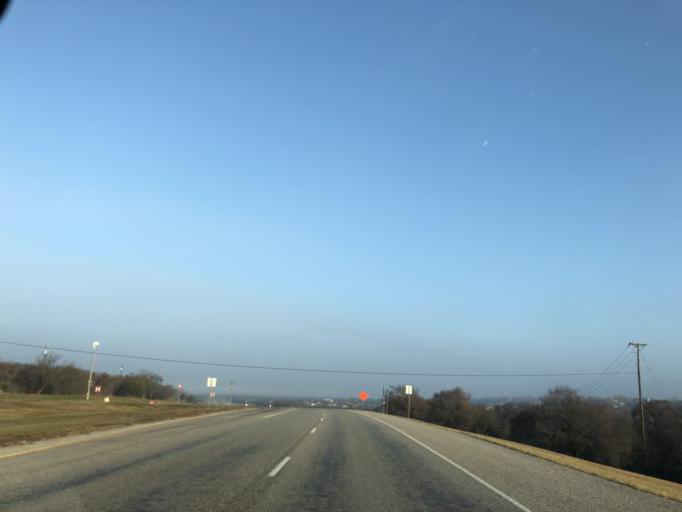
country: US
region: Texas
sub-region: Dallas County
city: Cedar Hill
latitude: 32.6397
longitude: -96.9722
